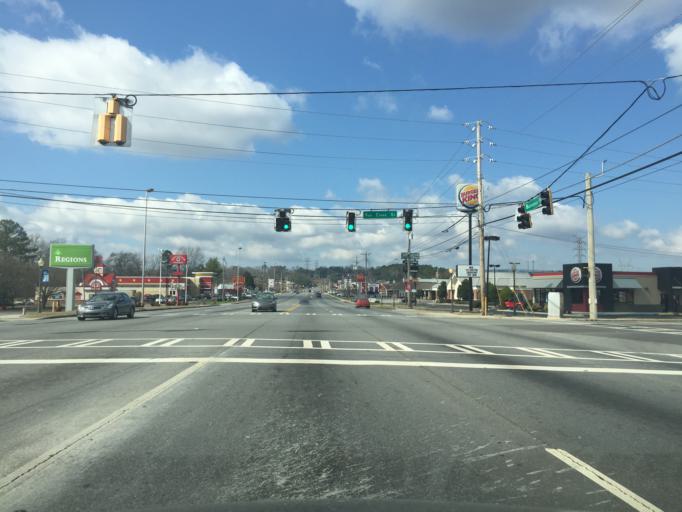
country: US
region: Georgia
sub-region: Catoosa County
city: Fort Oglethorpe
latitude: 34.9537
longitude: -85.2501
